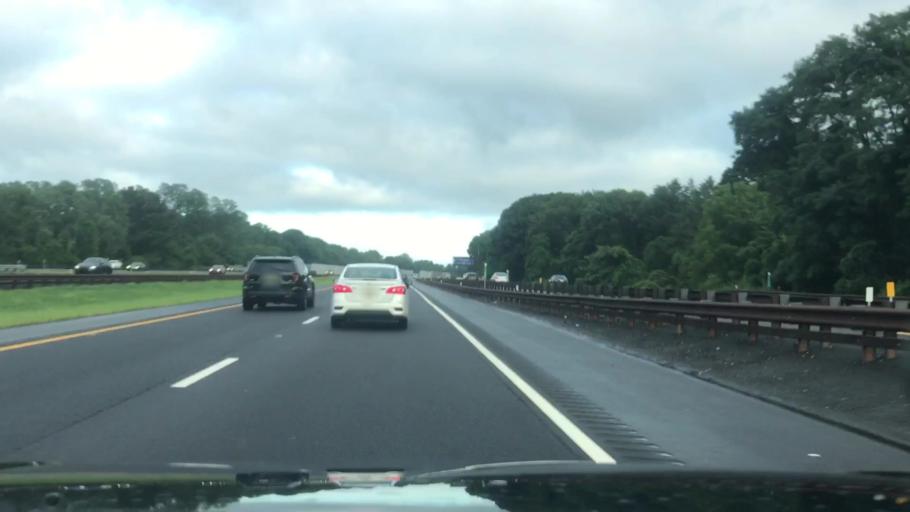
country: US
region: New Jersey
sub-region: Monmouth County
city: Lincroft
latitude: 40.3435
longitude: -74.1072
